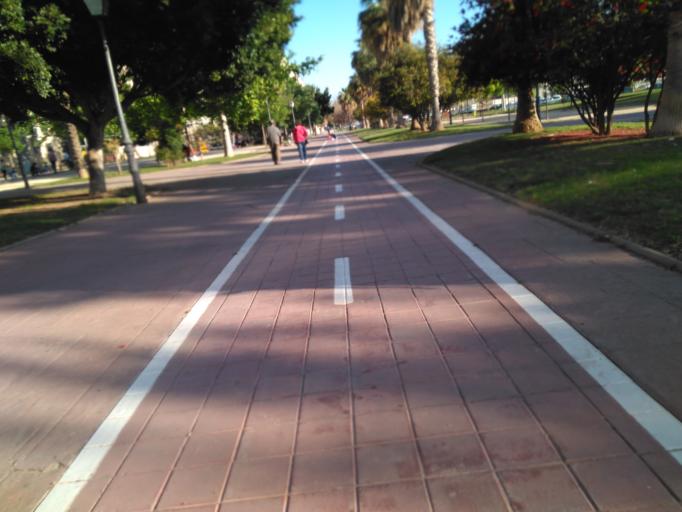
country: ES
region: Valencia
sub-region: Provincia de Valencia
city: Tavernes Blanques
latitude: 39.4961
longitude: -0.3857
